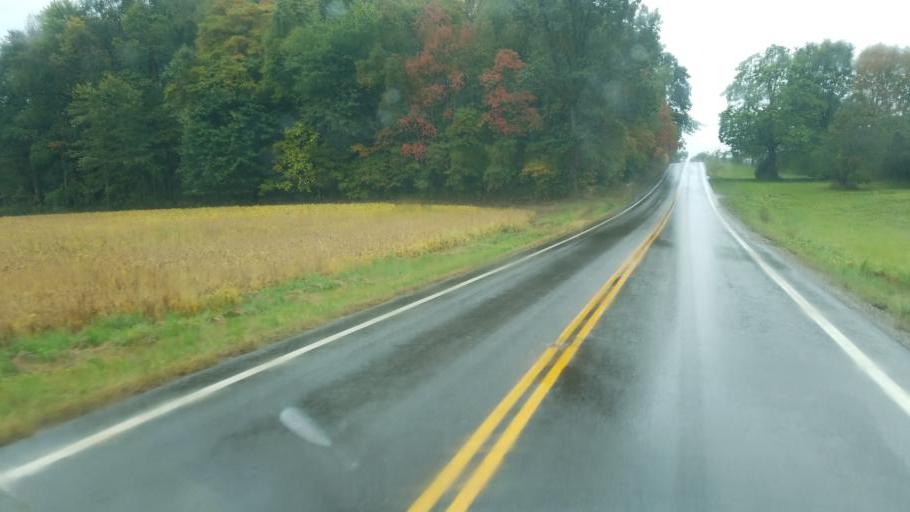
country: US
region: Ohio
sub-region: Richland County
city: Lincoln Heights
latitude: 40.6926
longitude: -82.3784
